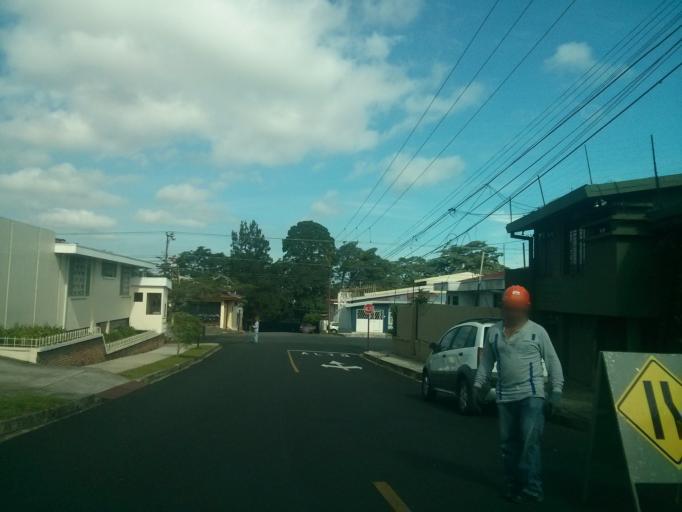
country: CR
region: San Jose
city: San Pedro
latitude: 9.9278
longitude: -84.0490
